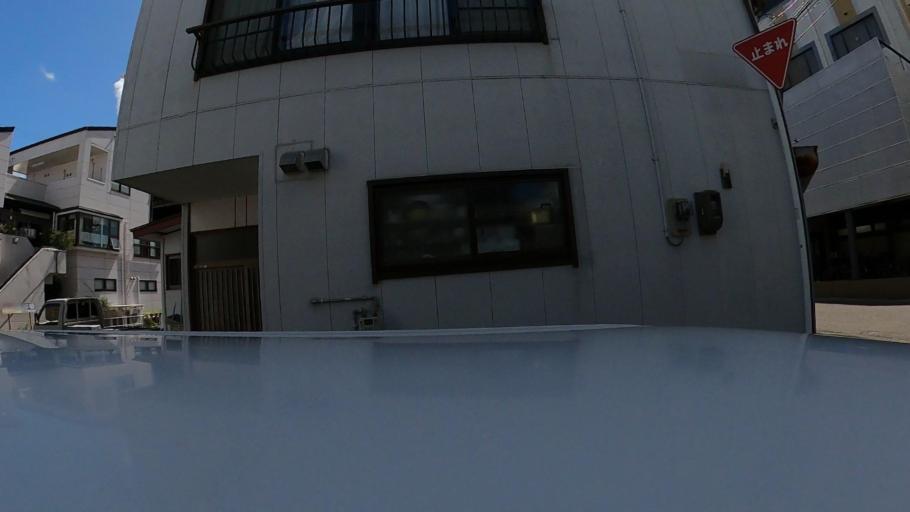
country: JP
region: Miyazaki
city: Tsuma
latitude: 32.1110
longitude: 131.4053
